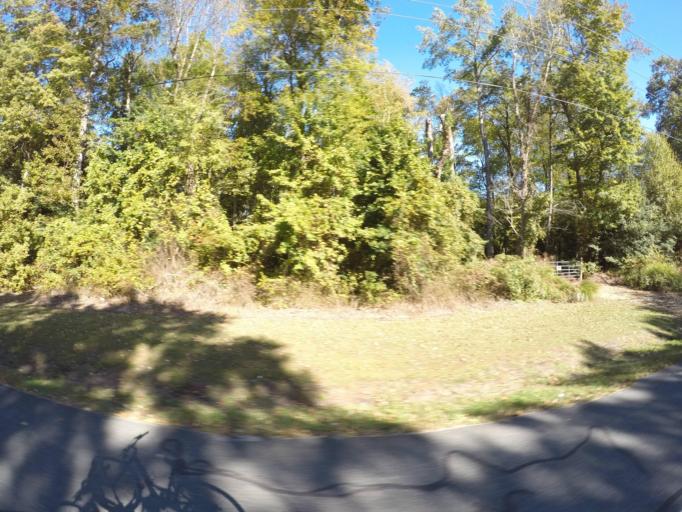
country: US
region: Delaware
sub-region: Sussex County
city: Bridgeville
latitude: 38.8062
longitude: -75.5085
